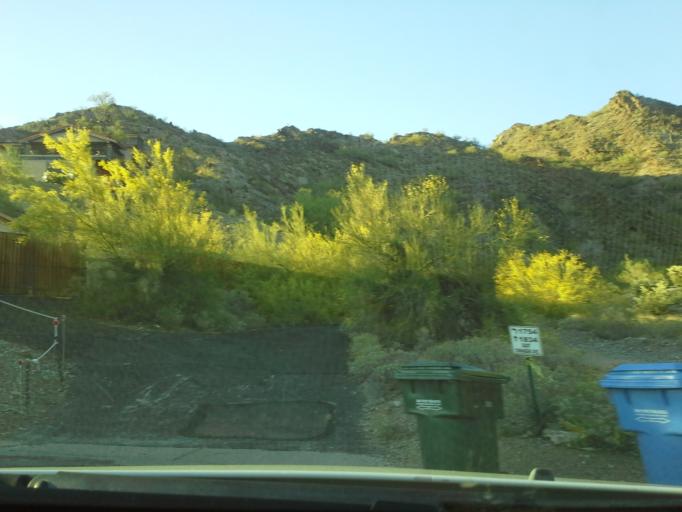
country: US
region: Arizona
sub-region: Maricopa County
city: Paradise Valley
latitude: 33.5775
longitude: -112.0435
